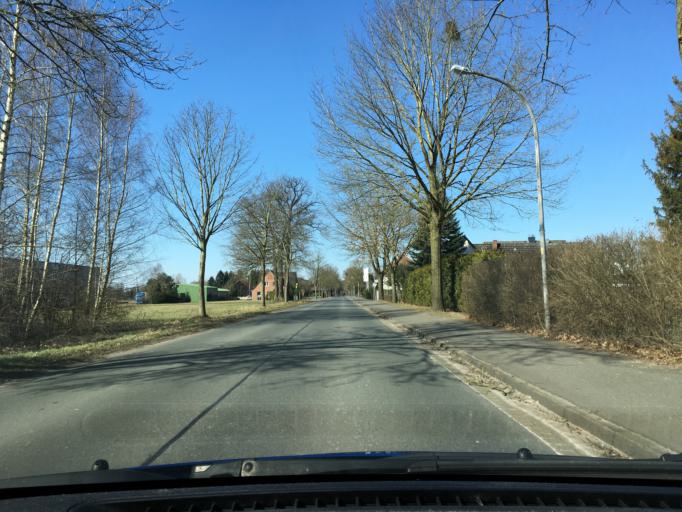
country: DE
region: Lower Saxony
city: Hemslingen
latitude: 53.0797
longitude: 9.6107
